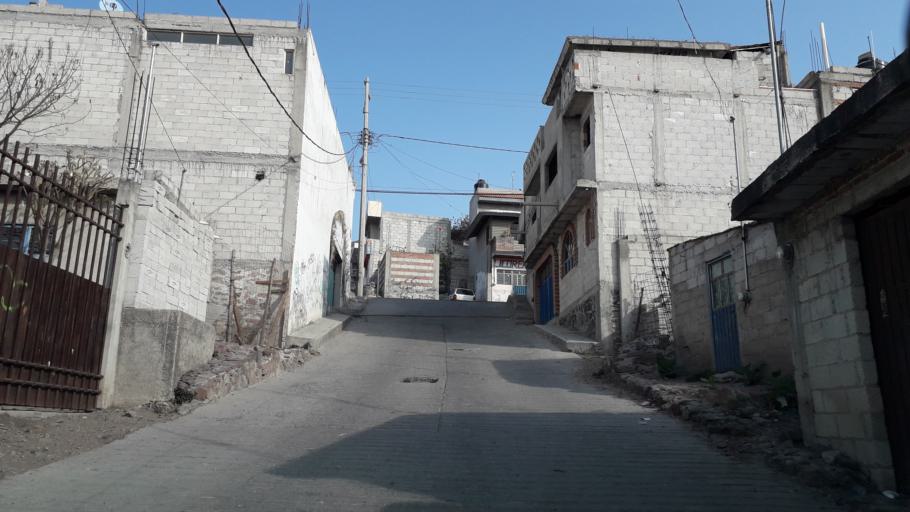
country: MX
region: Puebla
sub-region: Puebla
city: San Andres Azumiatla
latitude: 18.9024
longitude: -98.2533
